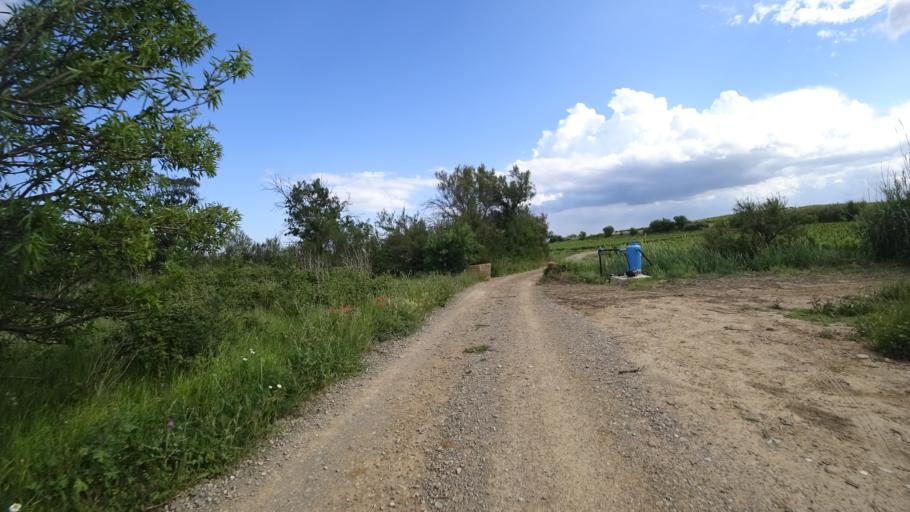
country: FR
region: Languedoc-Roussillon
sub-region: Departement de l'Aude
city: Ginestas
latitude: 43.2569
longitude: 2.8773
